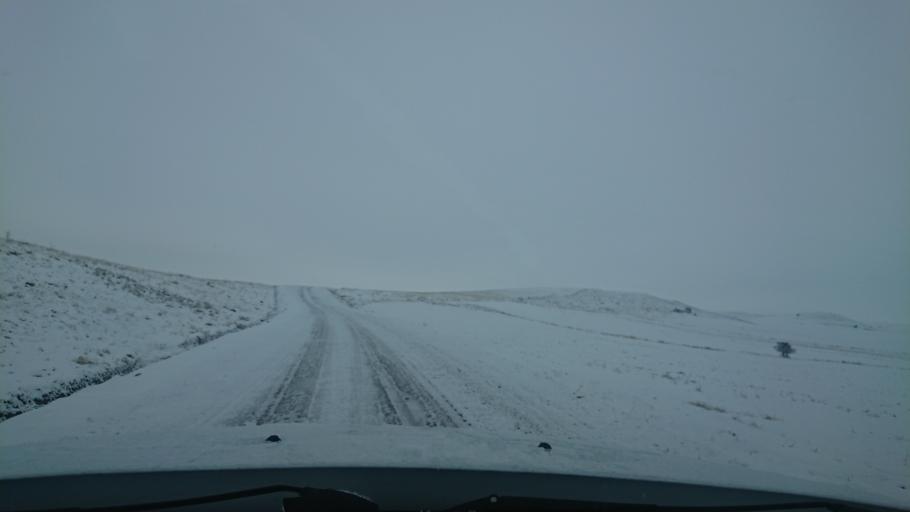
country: TR
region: Aksaray
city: Acipinar
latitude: 38.6874
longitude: 33.8697
